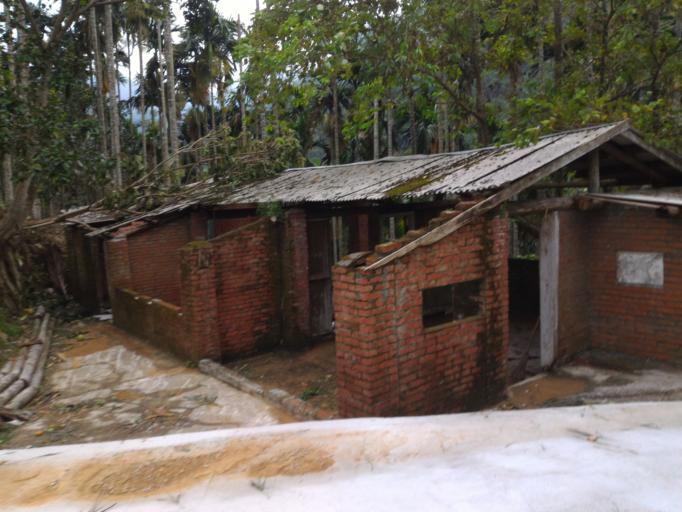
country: TW
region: Taipei
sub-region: Taipei
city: Banqiao
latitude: 24.9078
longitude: 121.4336
